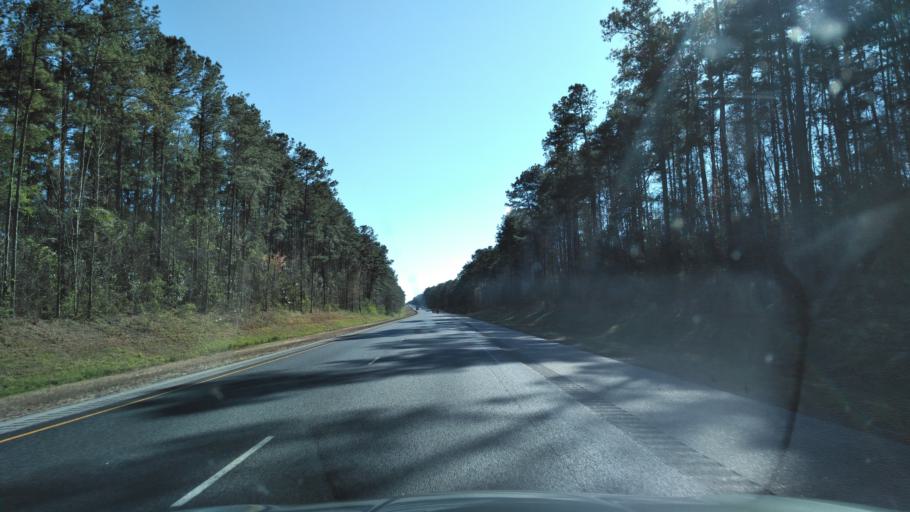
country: US
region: Alabama
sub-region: Butler County
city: Georgiana
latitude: 31.7070
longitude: -86.7374
